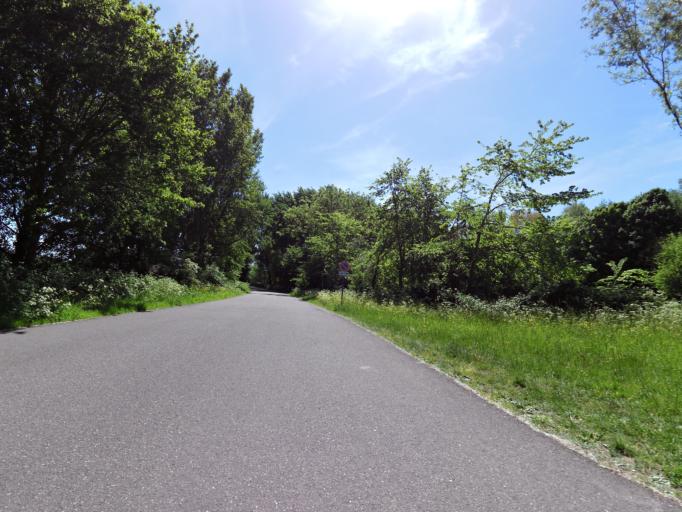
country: NL
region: South Holland
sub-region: Gemeente Hellevoetsluis
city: Nieuw-Helvoet
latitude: 51.8437
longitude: 4.0837
